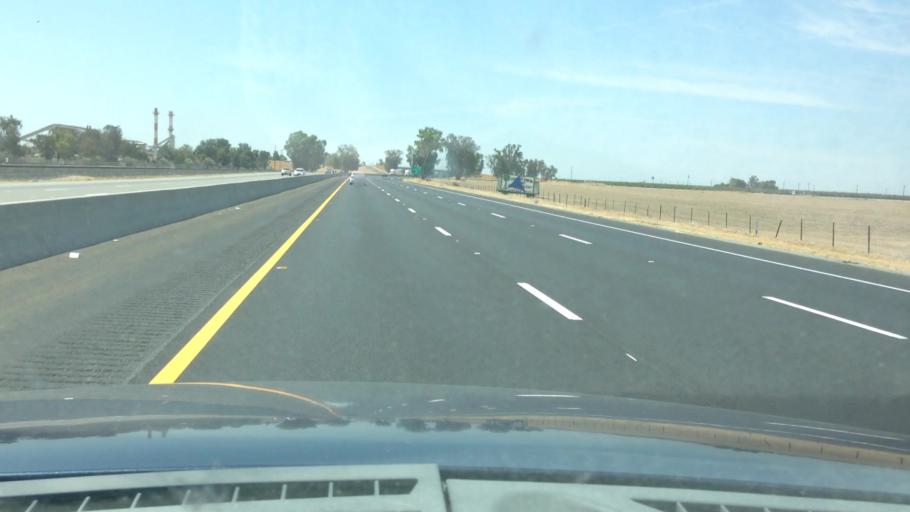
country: US
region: California
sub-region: Kern County
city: Delano
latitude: 35.7263
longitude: -119.2385
